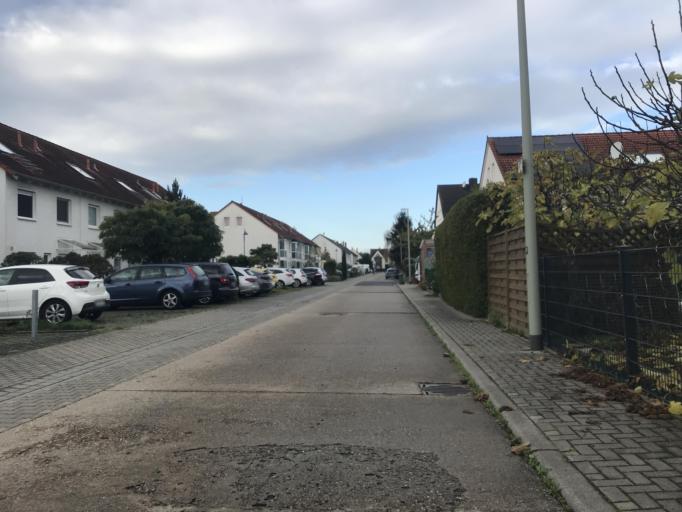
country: DE
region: Hesse
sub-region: Regierungsbezirk Darmstadt
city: Hochheim am Main
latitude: 50.0029
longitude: 8.3546
